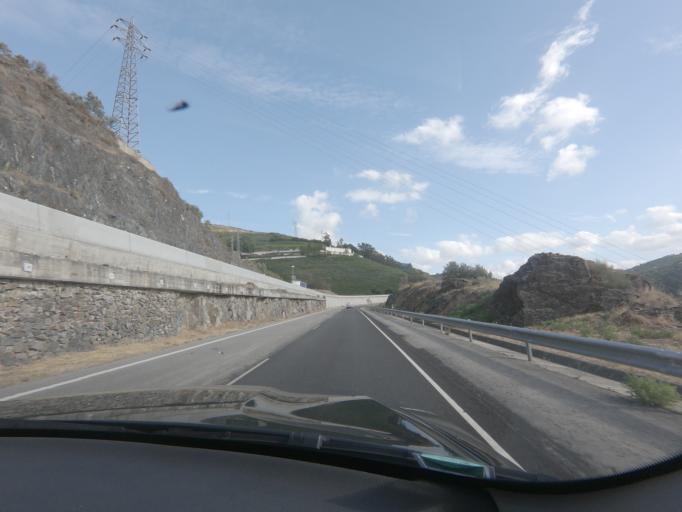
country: PT
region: Vila Real
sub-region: Peso da Regua
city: Peso da Regua
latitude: 41.1417
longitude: -7.7731
